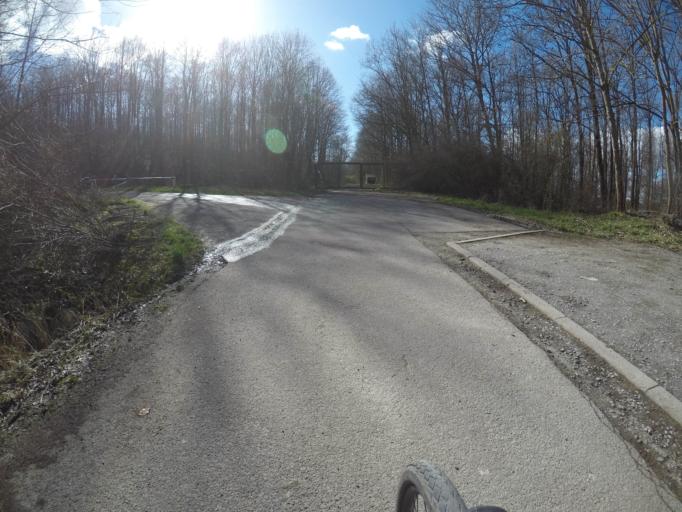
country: DE
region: Baden-Wuerttemberg
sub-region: Regierungsbezirk Stuttgart
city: Leinfelden-Echterdingen
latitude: 48.6865
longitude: 9.1418
